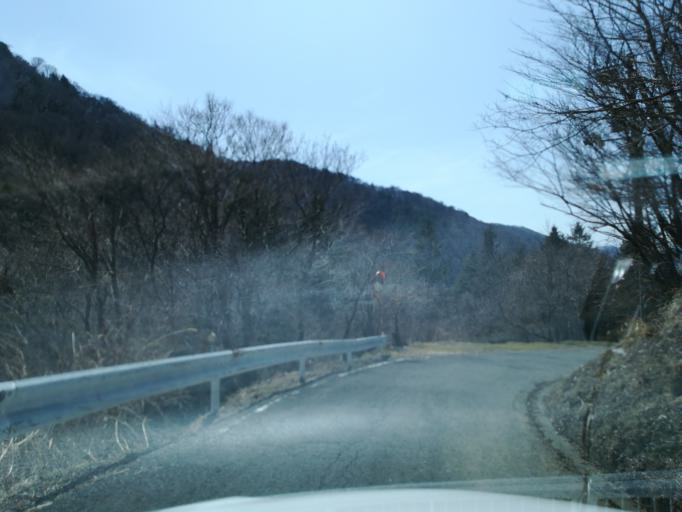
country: JP
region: Tokushima
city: Wakimachi
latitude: 33.8670
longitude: 134.0835
